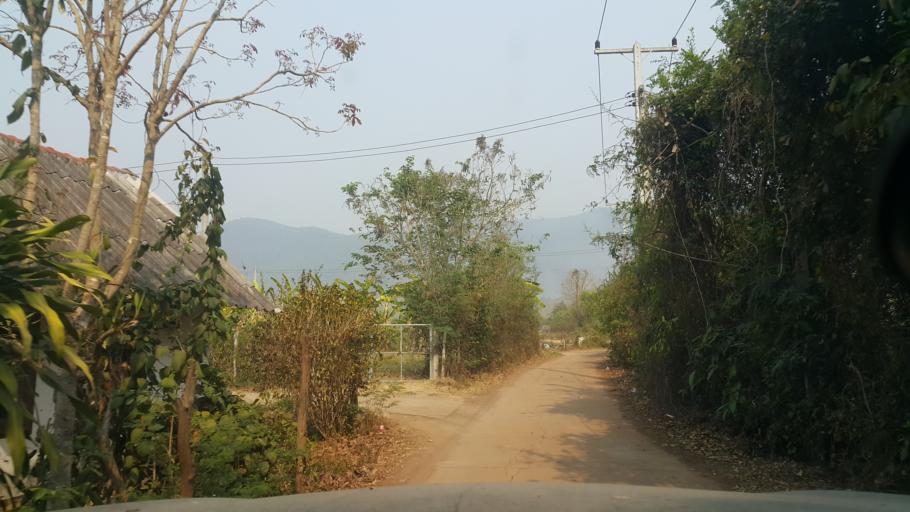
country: TH
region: Chiang Mai
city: Mae On
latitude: 18.7618
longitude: 99.2620
